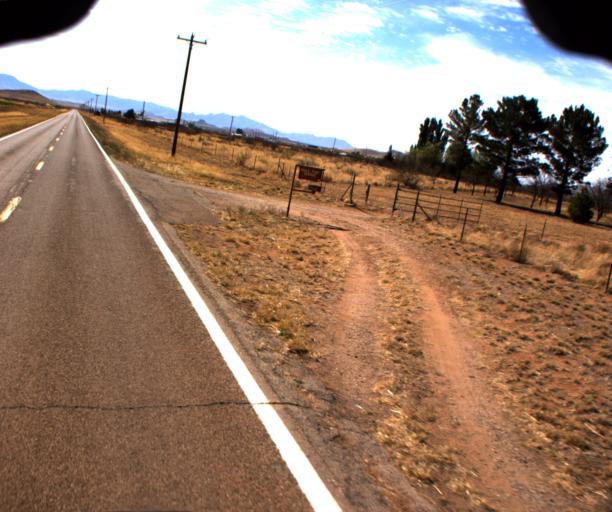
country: US
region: Arizona
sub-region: Cochise County
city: Willcox
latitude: 31.8765
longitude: -109.6451
